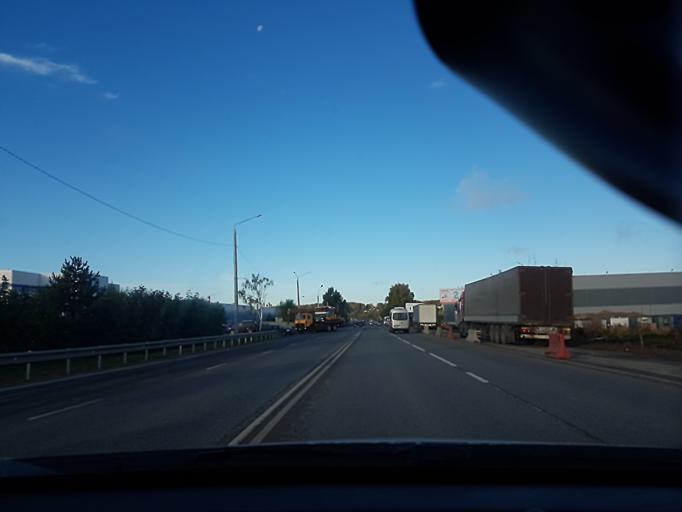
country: RU
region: Moskovskaya
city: Pavlovskaya Sloboda
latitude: 55.8150
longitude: 37.0667
